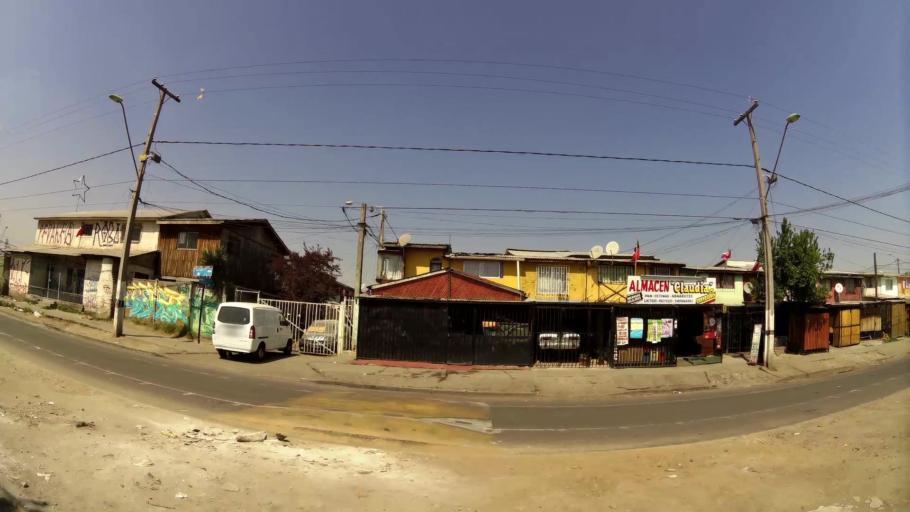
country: CL
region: Santiago Metropolitan
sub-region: Provincia de Santiago
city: La Pintana
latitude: -33.5556
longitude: -70.6128
